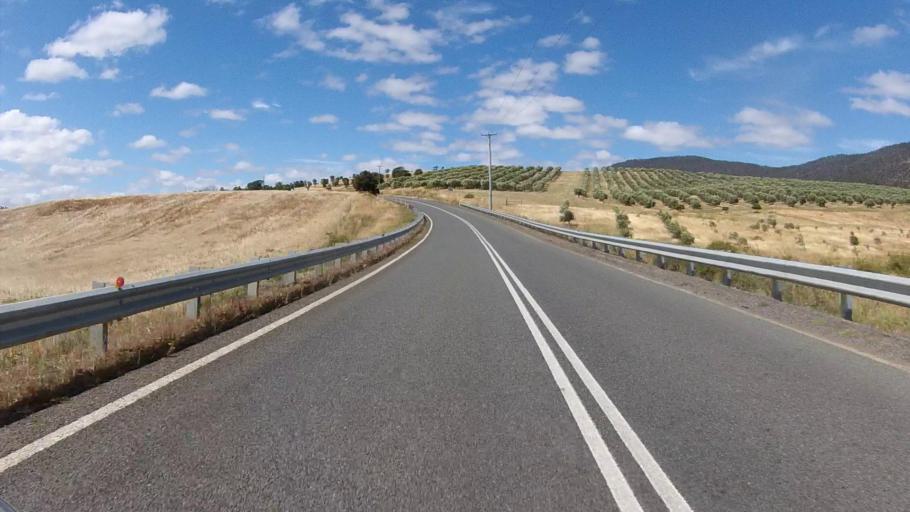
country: AU
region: Tasmania
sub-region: Brighton
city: Old Beach
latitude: -42.6031
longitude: 147.4170
